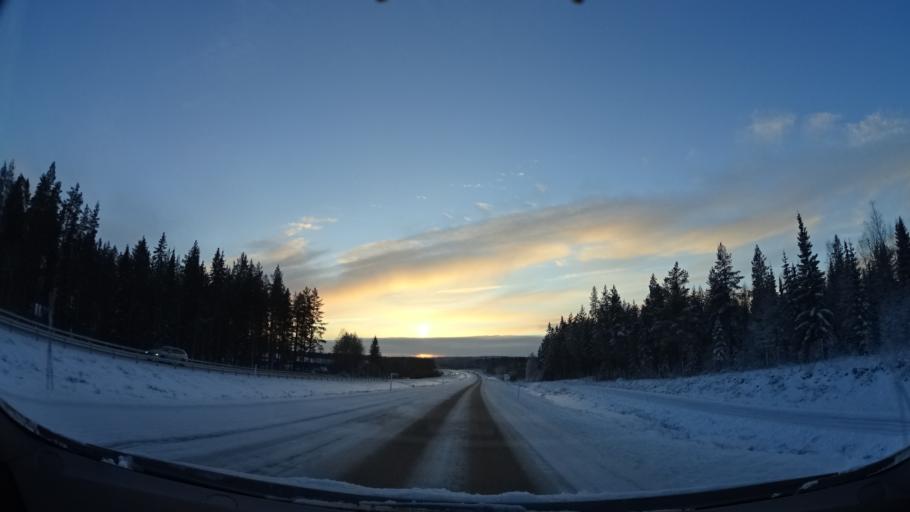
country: SE
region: Vaesterbotten
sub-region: Skelleftea Kommun
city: Kage
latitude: 64.8015
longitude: 21.0297
